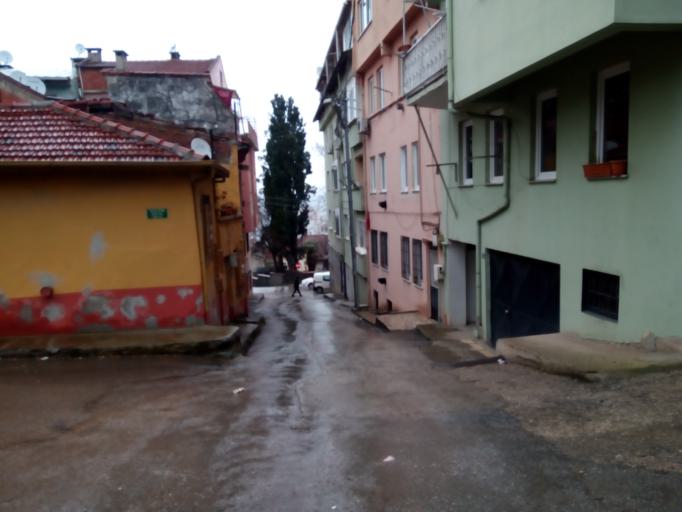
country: TR
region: Bursa
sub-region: Osmangazi
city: Bursa
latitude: 40.1794
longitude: 29.0574
